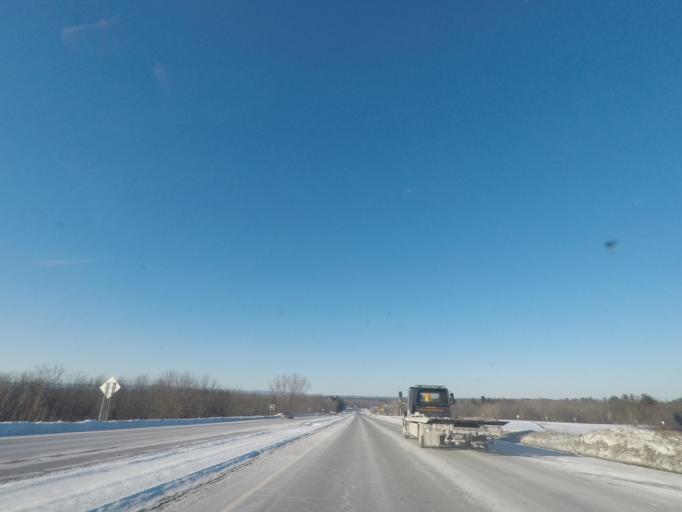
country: US
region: New York
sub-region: Saratoga County
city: North Ballston Spa
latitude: 43.0187
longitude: -73.7909
